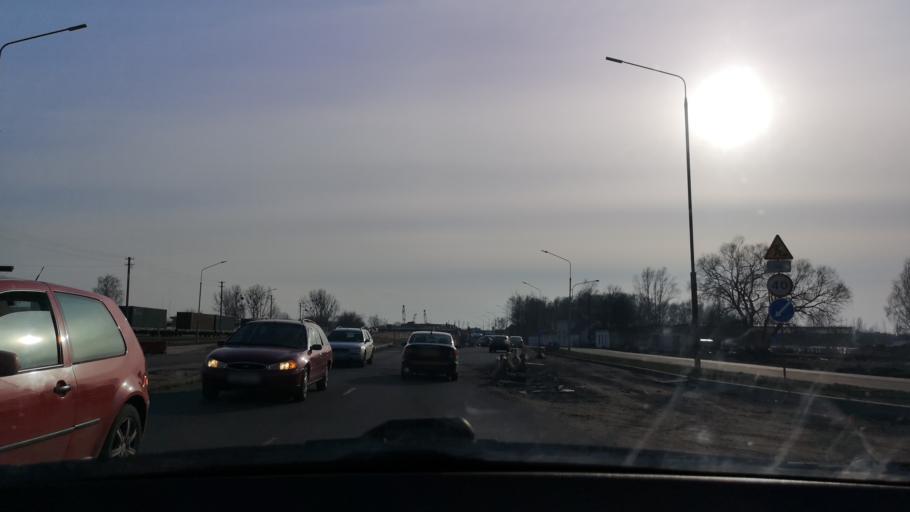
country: BY
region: Brest
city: Brest
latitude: 52.1112
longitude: 23.6677
